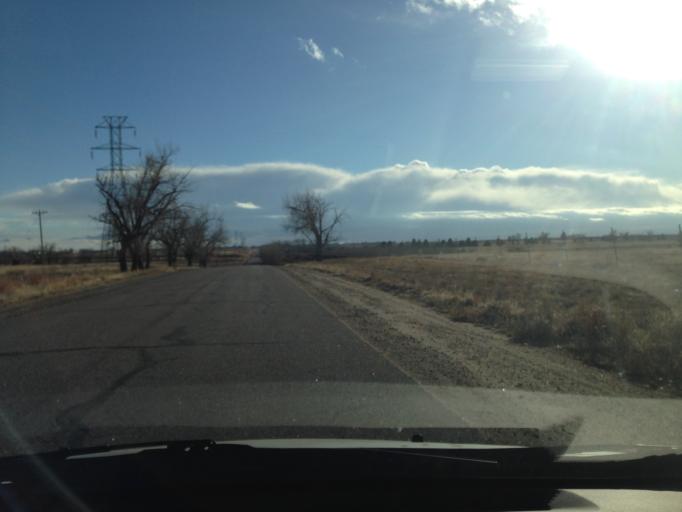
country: US
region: Colorado
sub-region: Adams County
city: Derby
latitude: 39.8242
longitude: -104.8658
